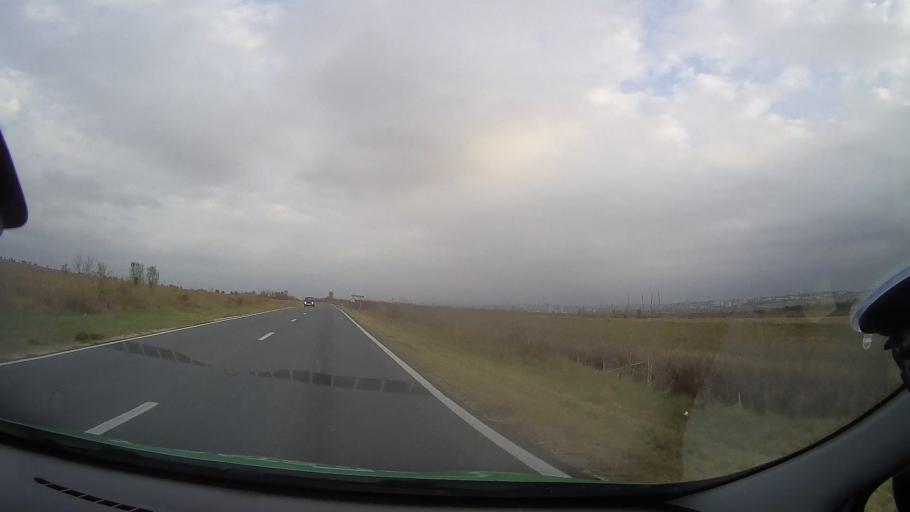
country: RO
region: Constanta
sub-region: Comuna Mircea Voda
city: Satu Nou
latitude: 44.2654
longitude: 28.2407
